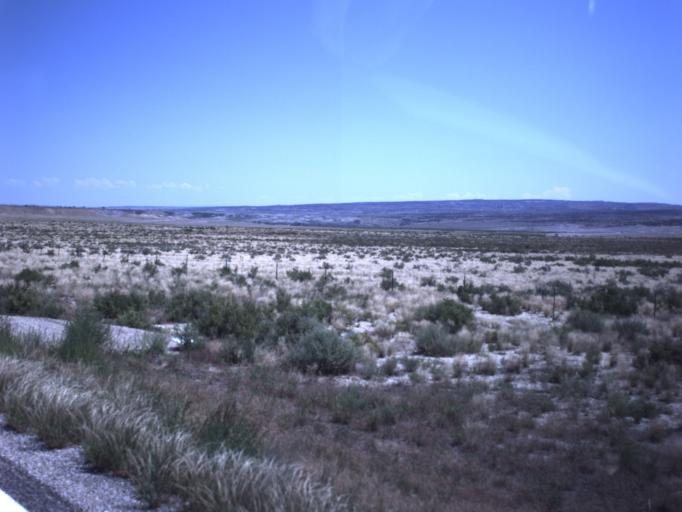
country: US
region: Utah
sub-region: Emery County
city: Ferron
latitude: 38.8431
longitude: -111.3132
